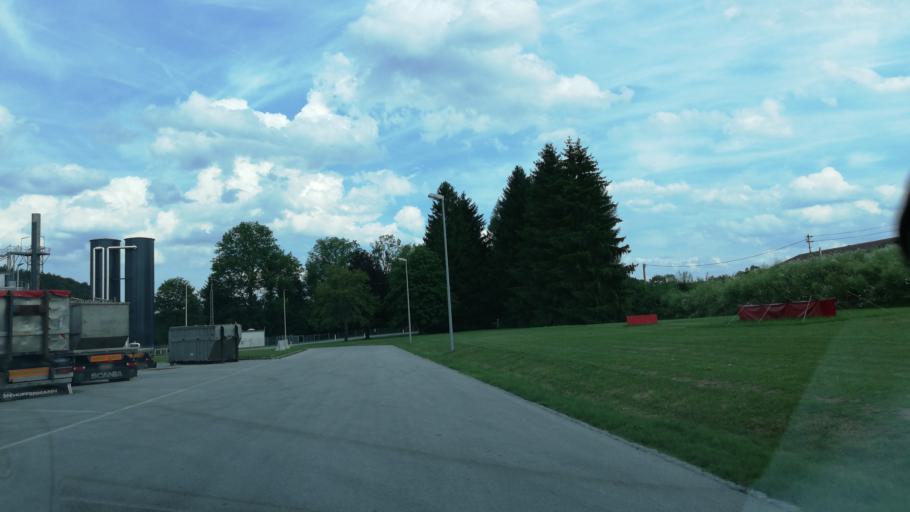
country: AT
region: Upper Austria
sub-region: Politischer Bezirk Vocklabruck
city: Attnang-Puchheim
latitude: 47.9946
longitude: 13.6946
